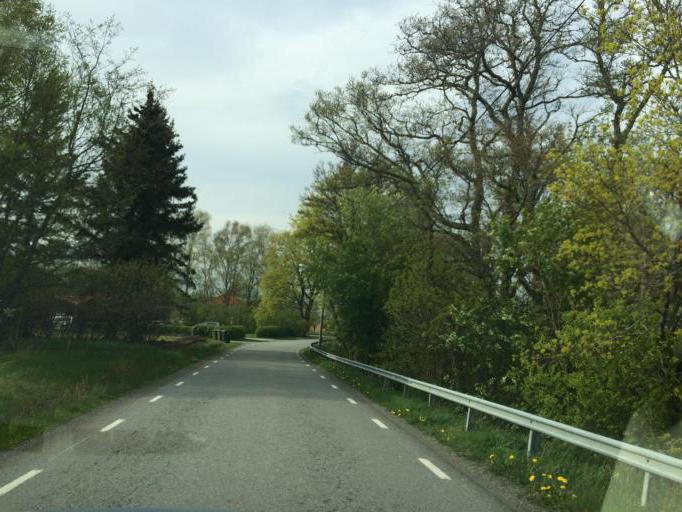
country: SE
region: Vaestmanland
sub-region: Kopings Kommun
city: Koping
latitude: 59.5769
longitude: 15.9877
